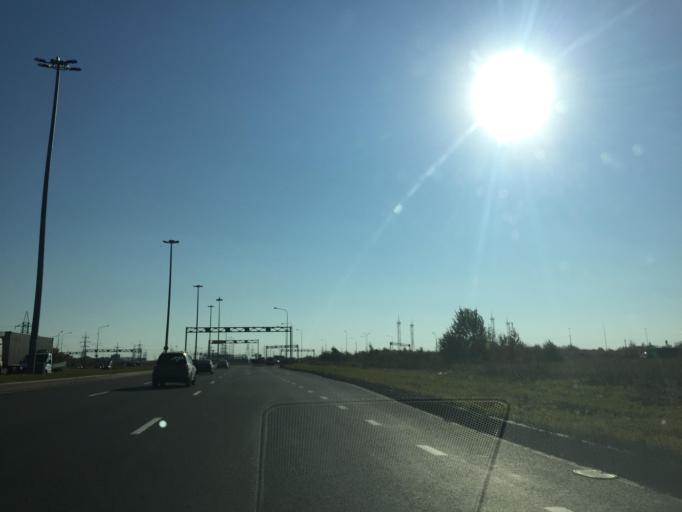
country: RU
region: St.-Petersburg
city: Metallostroy
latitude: 59.7505
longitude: 30.5279
